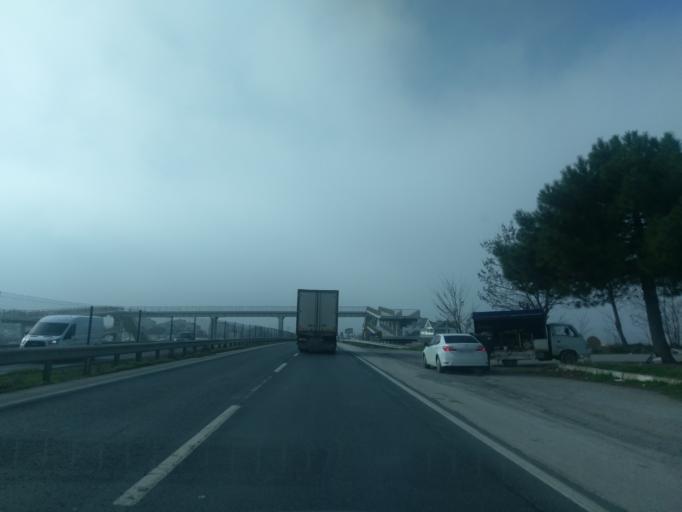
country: TR
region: Istanbul
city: Selimpasa
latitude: 41.0590
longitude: 28.3591
